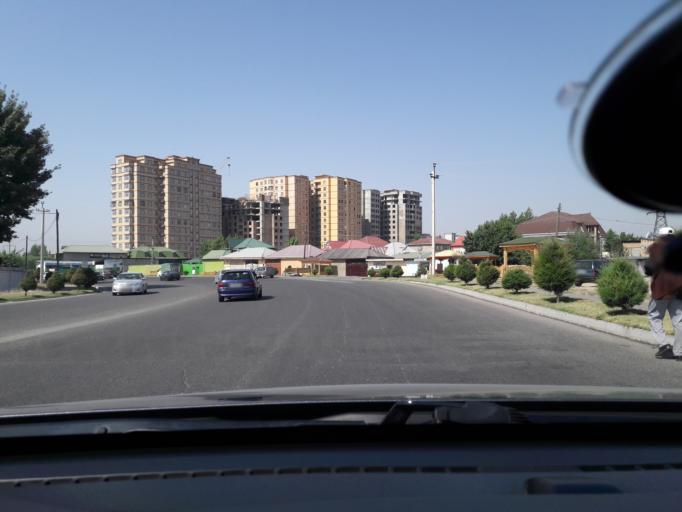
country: TJ
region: Dushanbe
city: Dushanbe
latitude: 38.5031
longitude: 68.7607
